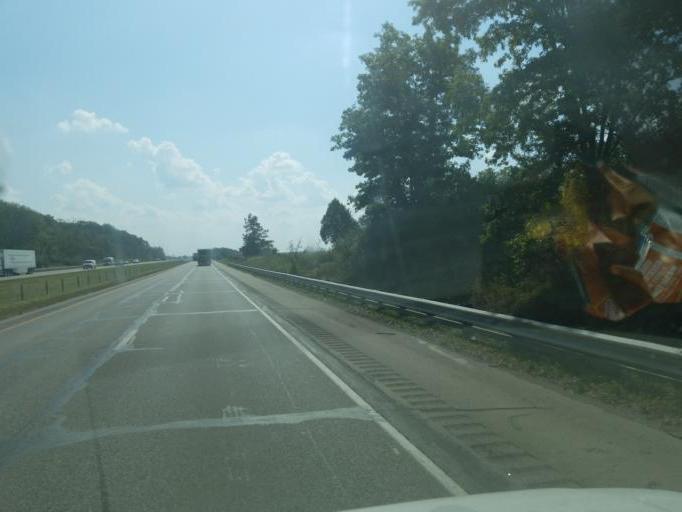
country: US
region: Indiana
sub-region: DeKalb County
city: Garrett
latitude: 41.3082
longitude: -85.0878
